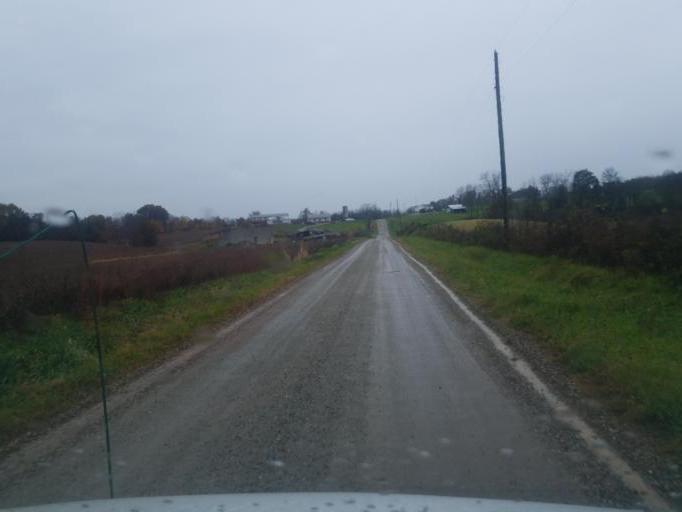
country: US
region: Ohio
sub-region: Washington County
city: Beverly
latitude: 39.4711
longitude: -81.6899
